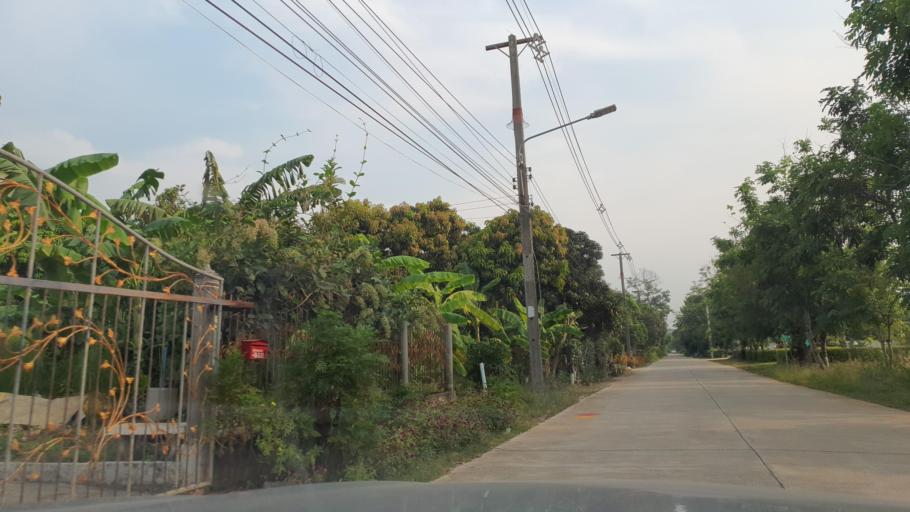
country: TH
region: Rayong
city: Rayong
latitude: 12.6096
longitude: 101.4007
